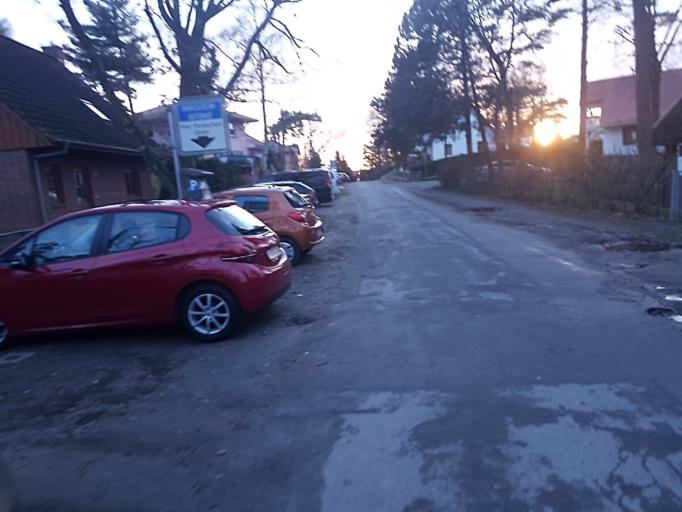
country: DE
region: Mecklenburg-Vorpommern
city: Ostseebad Binz
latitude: 54.4044
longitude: 13.6055
